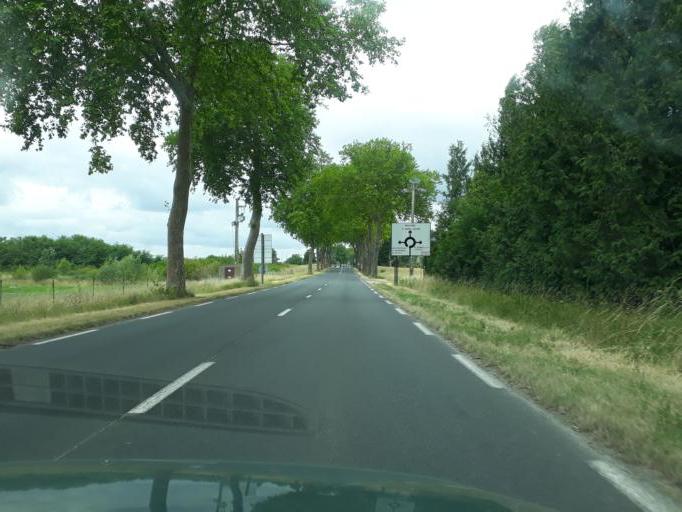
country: FR
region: Centre
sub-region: Departement du Loiret
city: Saint-Denis-en-Val
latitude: 47.8666
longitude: 1.9623
